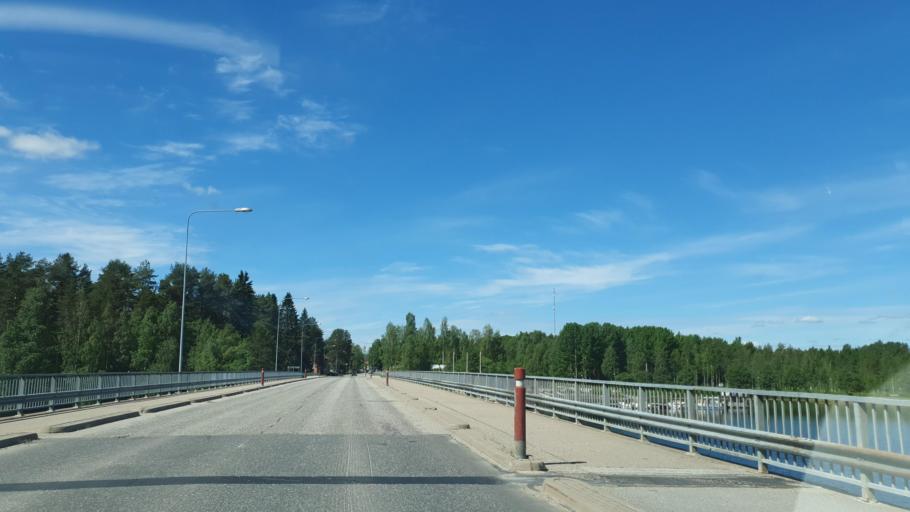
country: FI
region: Kainuu
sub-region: Kehys-Kainuu
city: Hyrynsalmi
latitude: 64.6749
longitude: 28.5033
